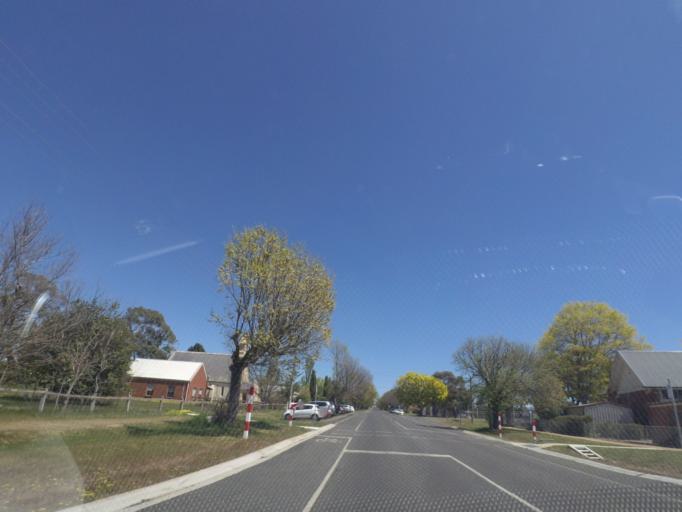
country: AU
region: Victoria
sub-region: Hume
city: Sunbury
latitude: -37.2791
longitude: 144.7322
